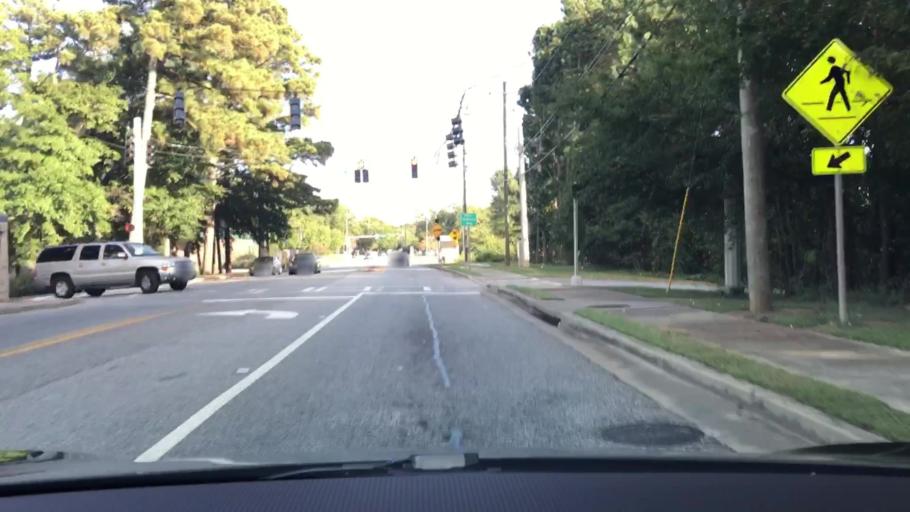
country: US
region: Georgia
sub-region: Gwinnett County
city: Dacula
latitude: 33.9936
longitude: -83.8993
